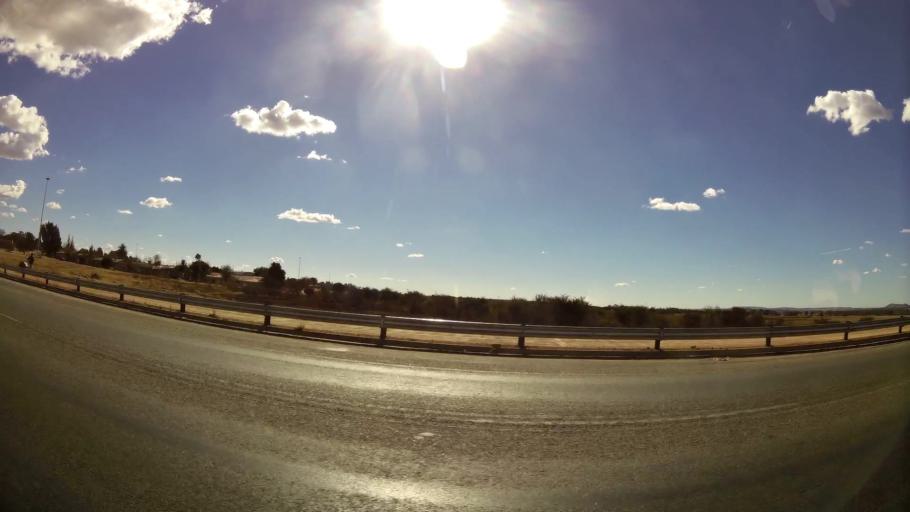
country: ZA
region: North-West
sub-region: Dr Kenneth Kaunda District Municipality
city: Klerksdorp
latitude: -26.8744
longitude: 26.5996
